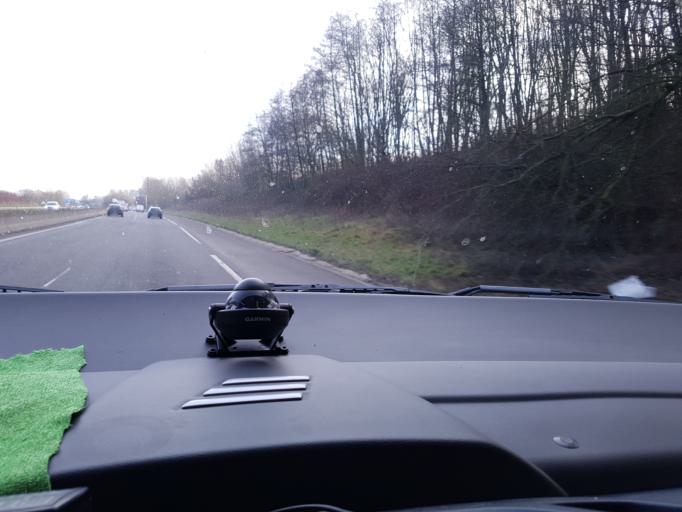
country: FR
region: Champagne-Ardenne
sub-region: Departement des Ardennes
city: La Francheville
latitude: 49.7440
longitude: 4.7058
